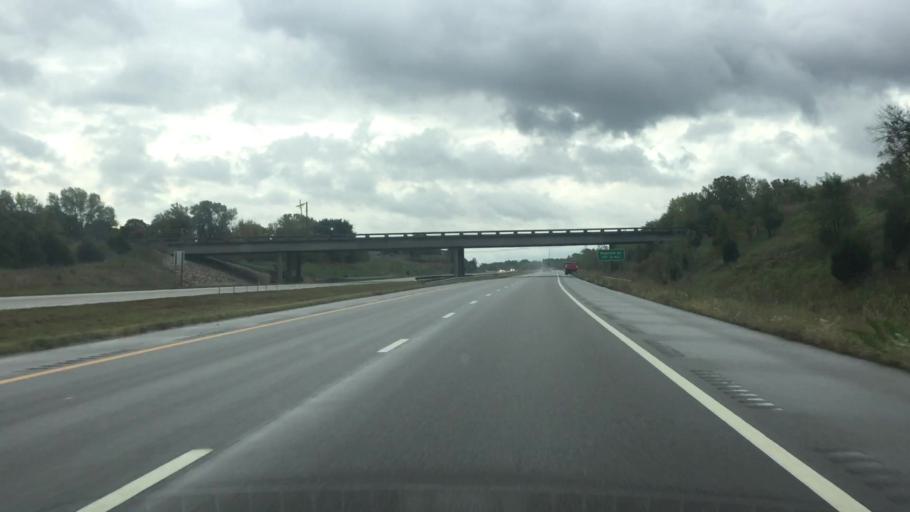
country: US
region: Kansas
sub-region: Miami County
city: Paola
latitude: 38.5617
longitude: -94.8629
